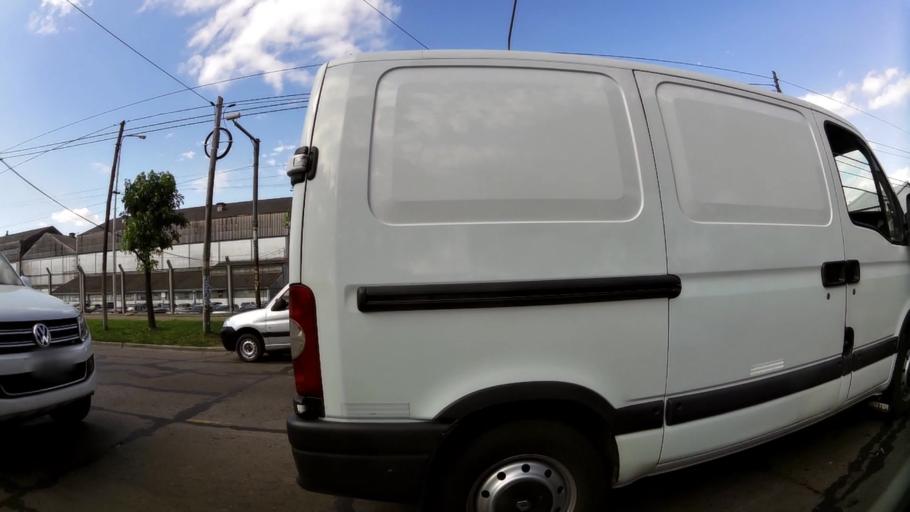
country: AR
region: Buenos Aires
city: San Justo
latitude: -34.6685
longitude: -58.5674
